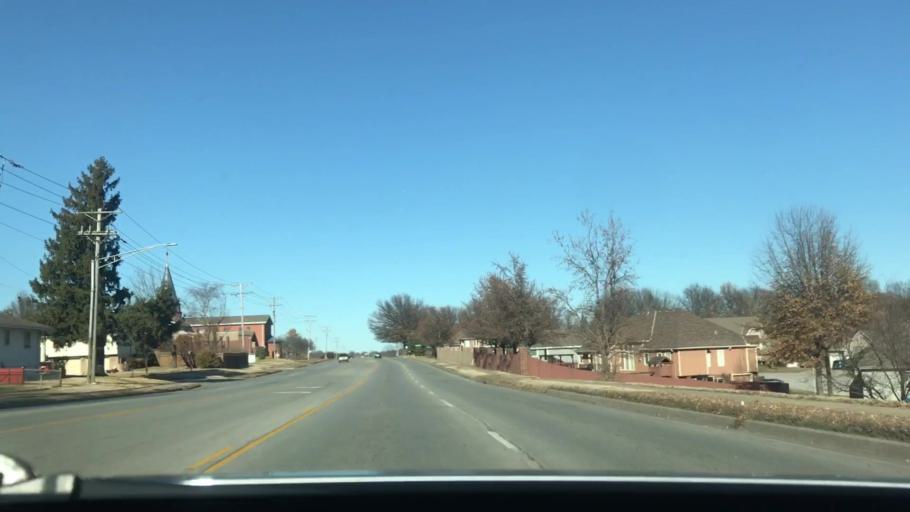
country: US
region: Missouri
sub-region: Jackson County
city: Independence
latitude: 39.0498
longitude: -94.3872
